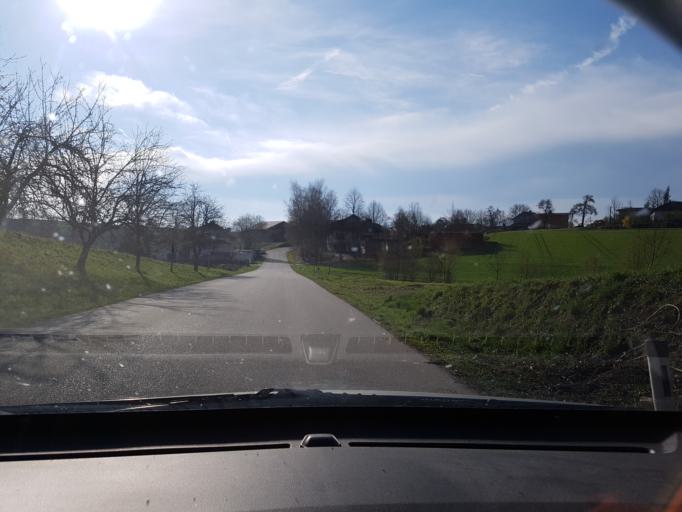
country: AT
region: Upper Austria
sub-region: Politischer Bezirk Linz-Land
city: Sankt Florian
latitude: 48.1543
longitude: 14.3863
